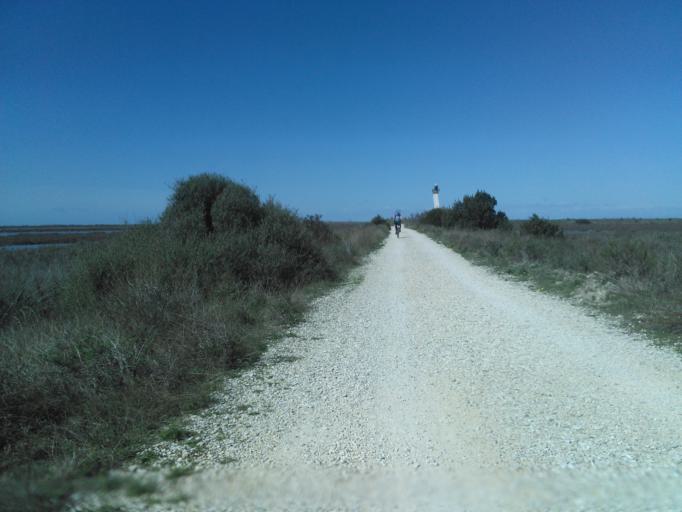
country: FR
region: Provence-Alpes-Cote d'Azur
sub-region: Departement des Bouches-du-Rhone
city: Saintes-Maries-de-la-Mer
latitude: 43.4545
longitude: 4.5749
